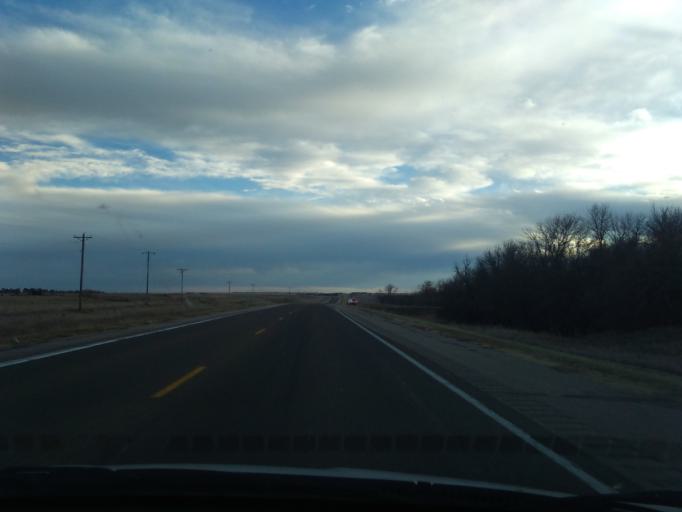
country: US
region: Nebraska
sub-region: Phelps County
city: Holdrege
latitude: 40.3669
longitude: -99.3693
